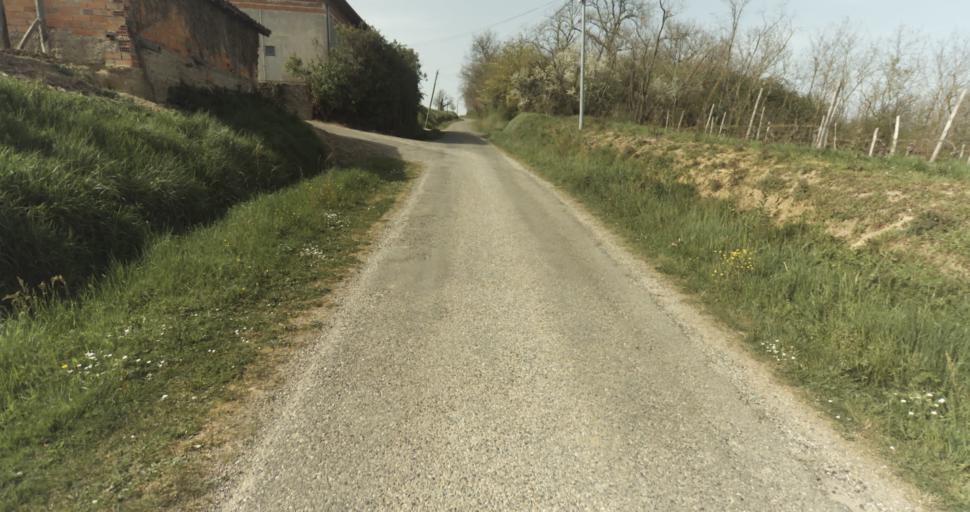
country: FR
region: Midi-Pyrenees
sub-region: Departement du Tarn-et-Garonne
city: Moissac
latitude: 44.1380
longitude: 1.1533
